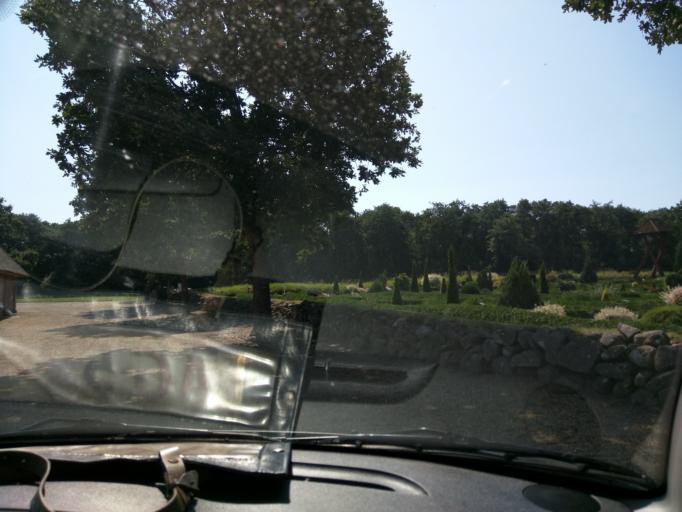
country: DK
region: Central Jutland
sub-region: Silkeborg Kommune
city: Svejbaek
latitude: 56.2436
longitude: 9.6747
